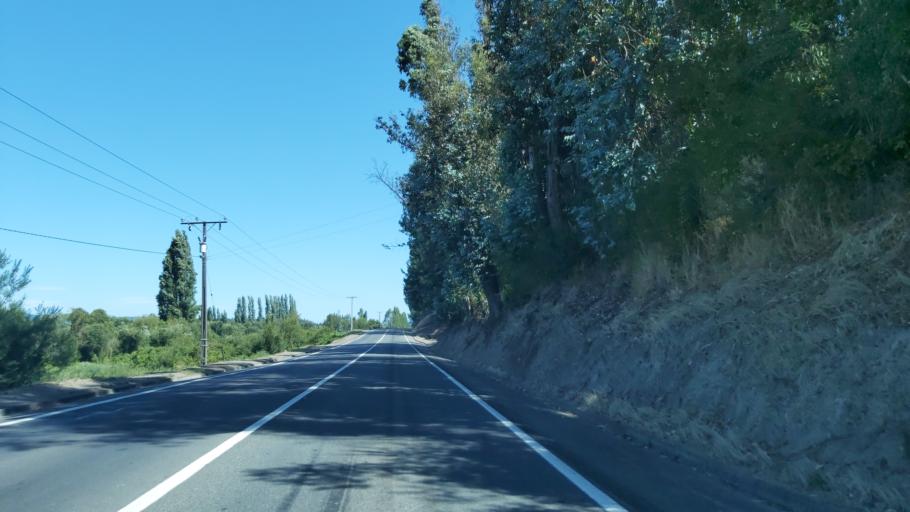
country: CL
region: Biobio
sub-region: Provincia de Concepcion
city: Lota
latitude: -37.1382
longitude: -72.9783
